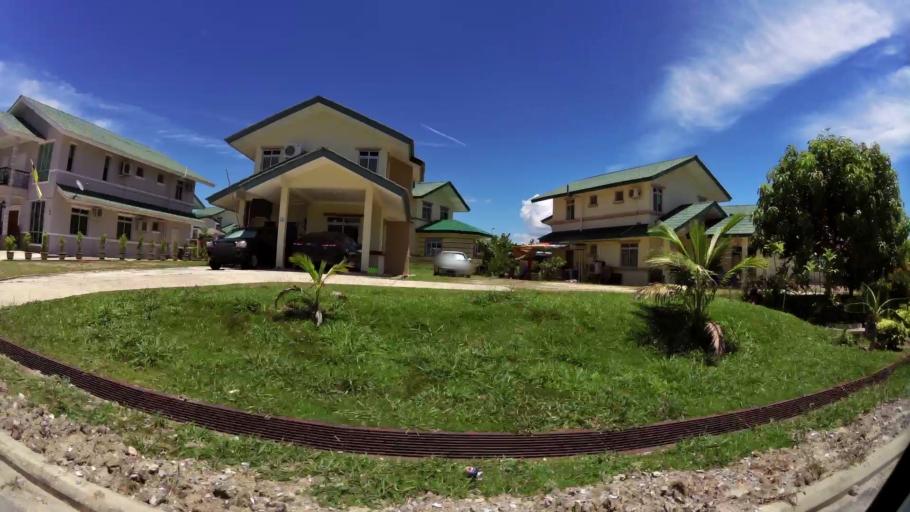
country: BN
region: Brunei and Muara
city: Bandar Seri Begawan
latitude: 5.0225
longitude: 115.0346
